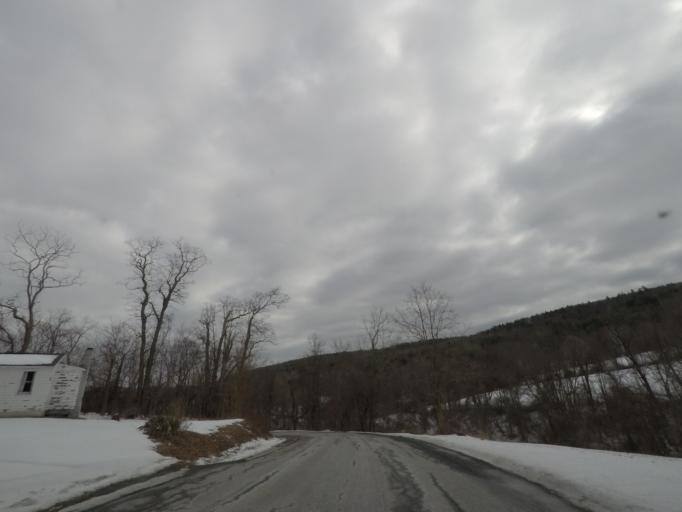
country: US
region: New York
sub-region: Rensselaer County
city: Hoosick Falls
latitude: 42.8658
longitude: -73.3838
